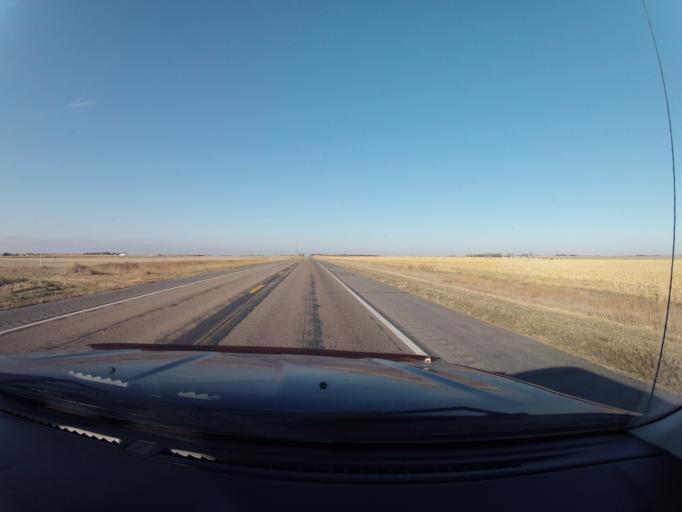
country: US
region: Nebraska
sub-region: Kearney County
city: Minden
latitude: 40.5588
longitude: -98.9518
